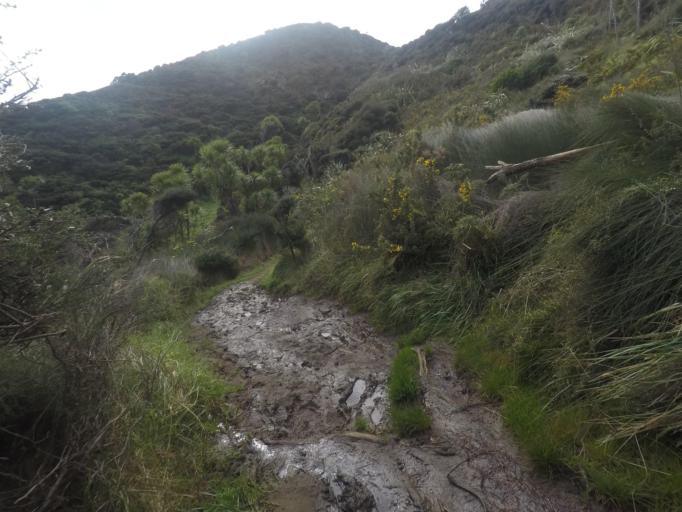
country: NZ
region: Auckland
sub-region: Auckland
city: Muriwai Beach
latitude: -36.8784
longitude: 174.4317
